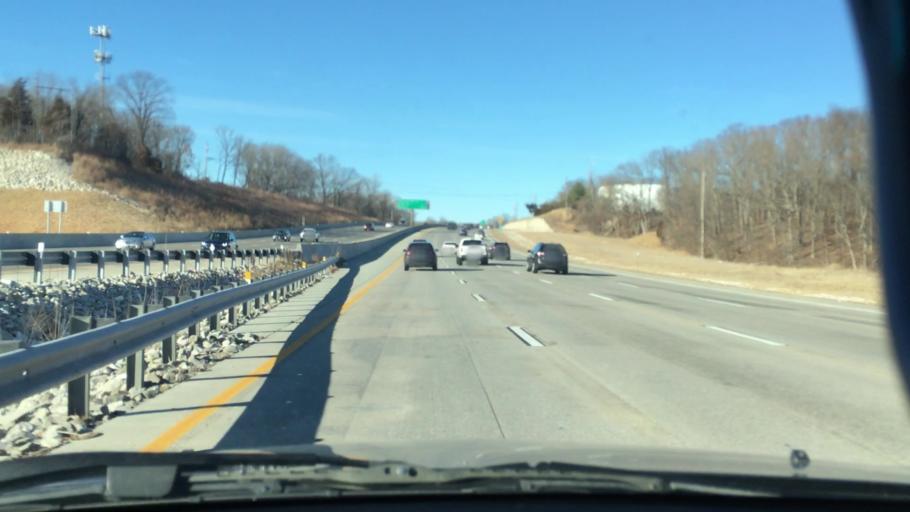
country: US
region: Missouri
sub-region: Saint Charles County
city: Weldon Spring
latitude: 38.6910
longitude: -90.6644
